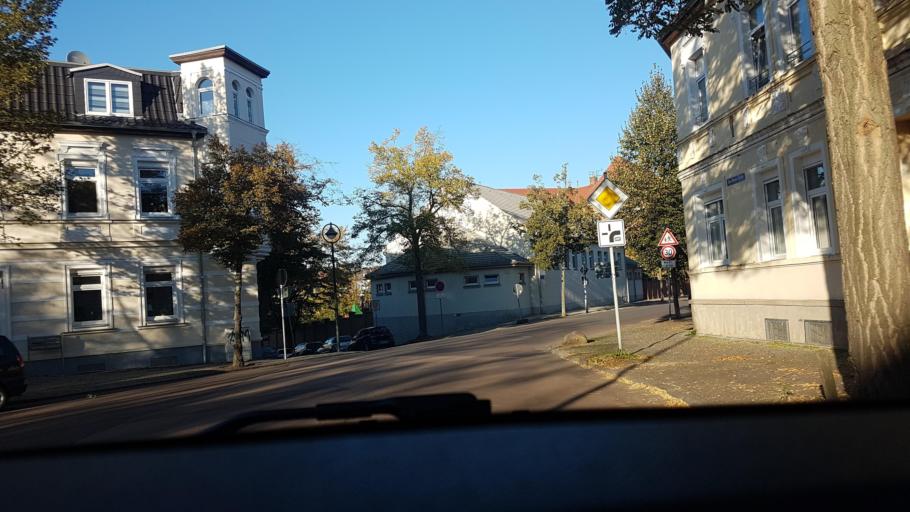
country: DE
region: Saxony-Anhalt
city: Bernburg
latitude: 51.7906
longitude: 11.7343
